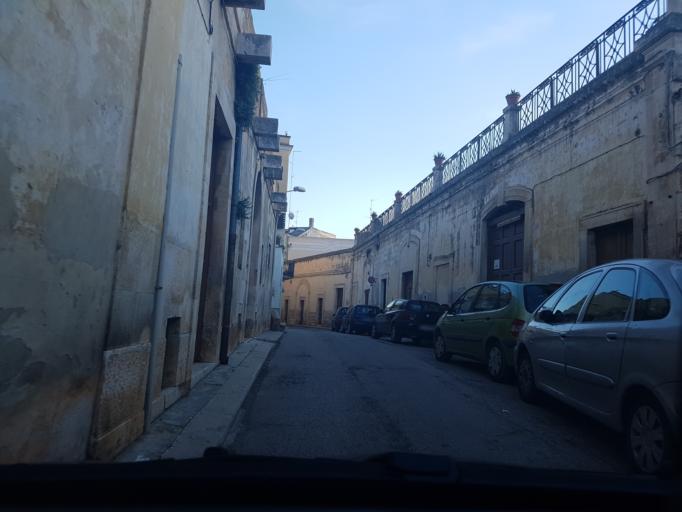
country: IT
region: Apulia
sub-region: Provincia di Bari
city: Bitritto
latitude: 41.0410
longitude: 16.8250
